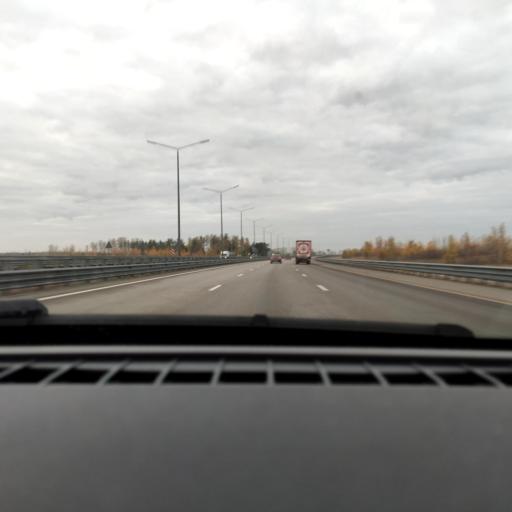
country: RU
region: Voronezj
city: Somovo
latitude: 51.7645
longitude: 39.3065
